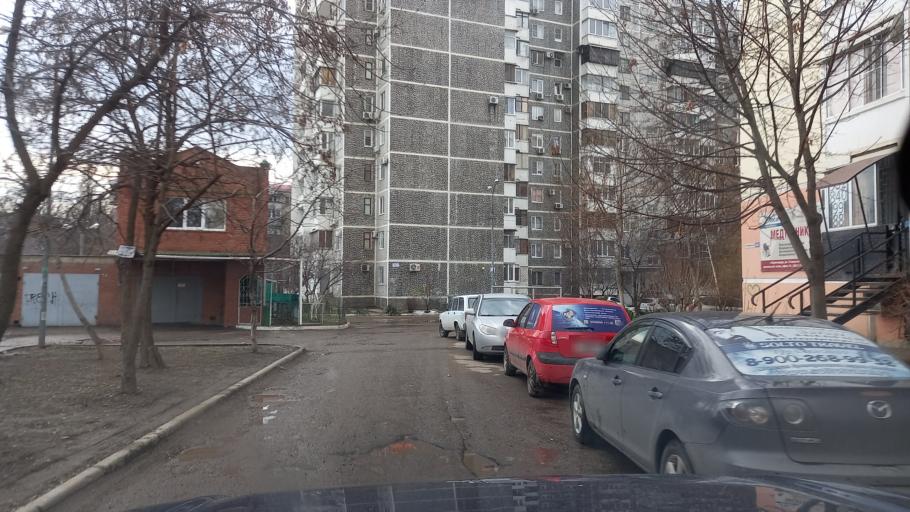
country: RU
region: Krasnodarskiy
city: Pashkovskiy
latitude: 45.0192
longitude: 39.0404
